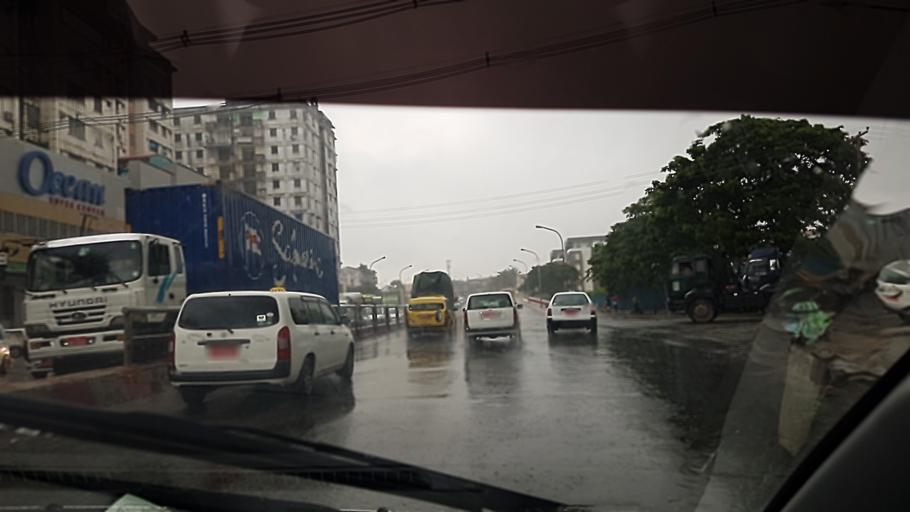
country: MM
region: Yangon
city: Yangon
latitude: 16.7736
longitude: 96.1779
